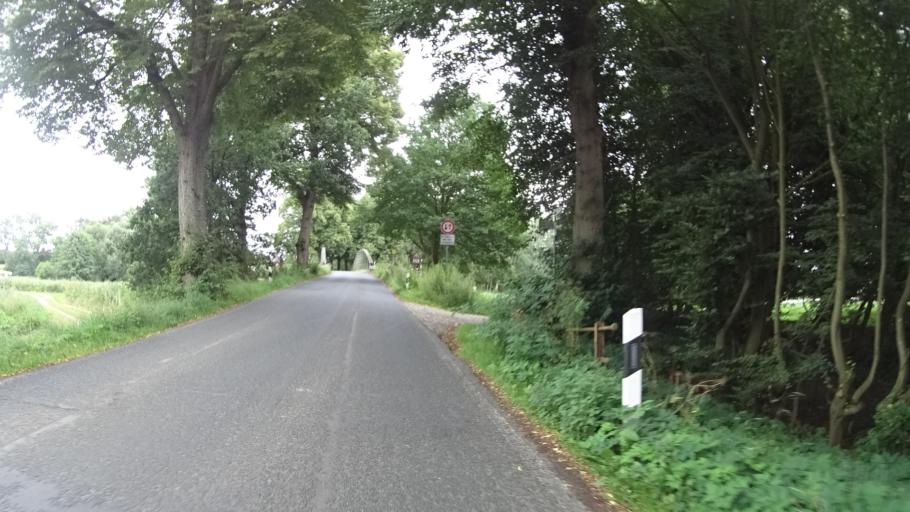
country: DE
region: Schleswig-Holstein
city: Kuhsen
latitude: 53.6854
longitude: 10.6318
